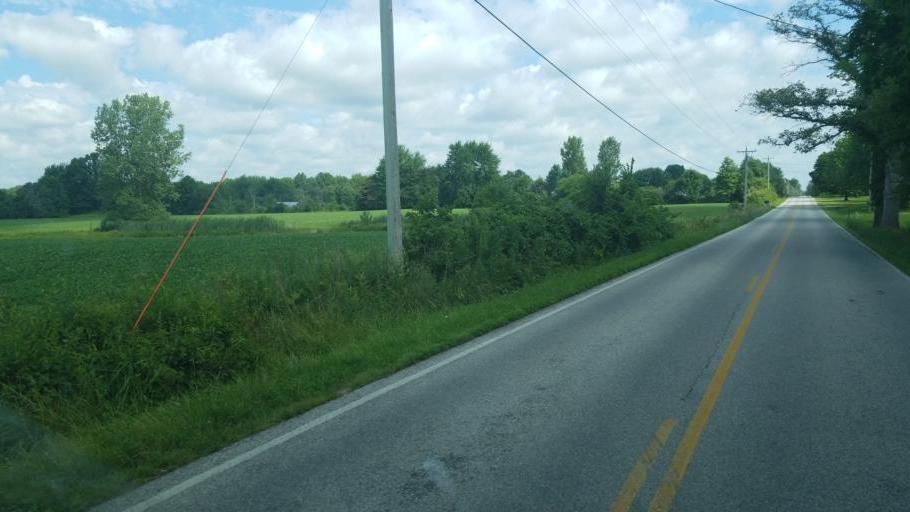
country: US
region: Ohio
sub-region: Delaware County
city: Sunbury
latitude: 40.2908
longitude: -82.9351
